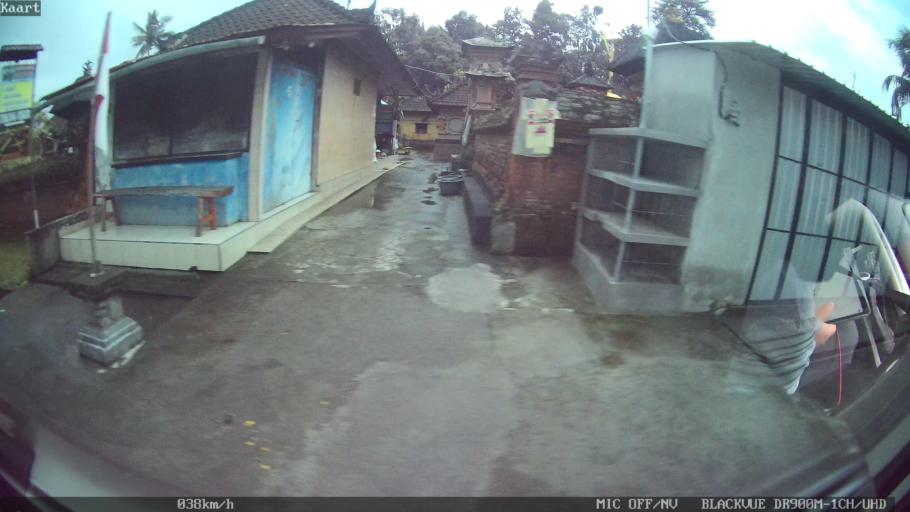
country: ID
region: Bali
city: Pegongan
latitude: -8.4849
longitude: 115.2267
